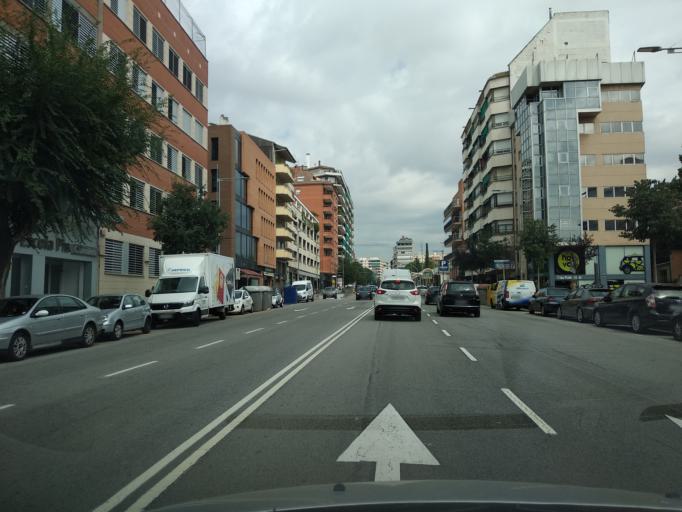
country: ES
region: Catalonia
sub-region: Provincia de Barcelona
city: Granollers
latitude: 41.6046
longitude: 2.2905
